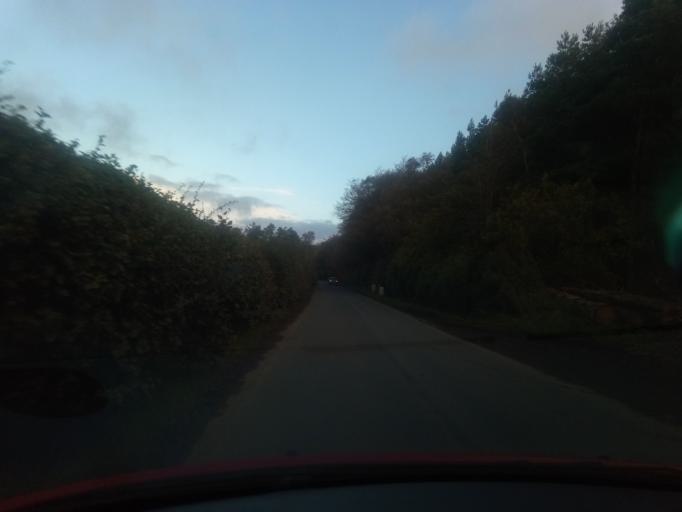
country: GB
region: Scotland
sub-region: The Scottish Borders
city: Jedburgh
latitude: 55.3858
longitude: -2.6430
